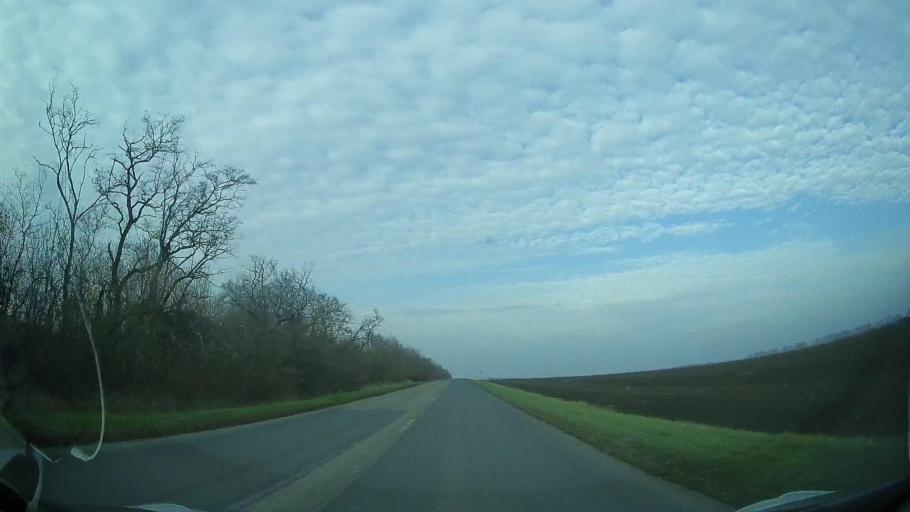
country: RU
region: Rostov
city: Bagayevskaya
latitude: 47.0786
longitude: 40.3915
